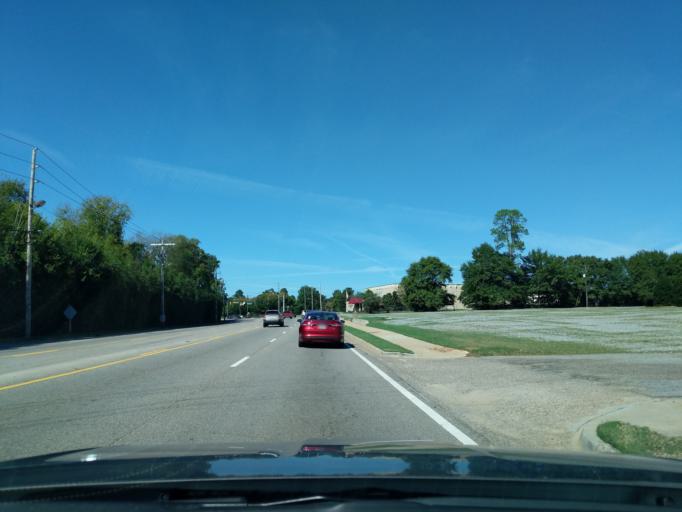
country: US
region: South Carolina
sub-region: Aiken County
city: North Augusta
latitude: 33.5034
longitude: -82.0153
